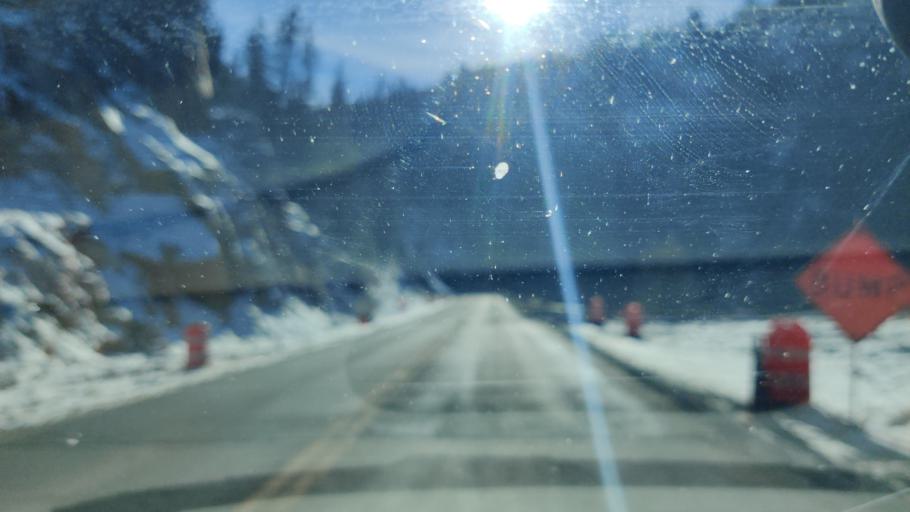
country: US
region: Colorado
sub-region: Hinsdale County
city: Lake City
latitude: 38.4154
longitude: -107.4065
